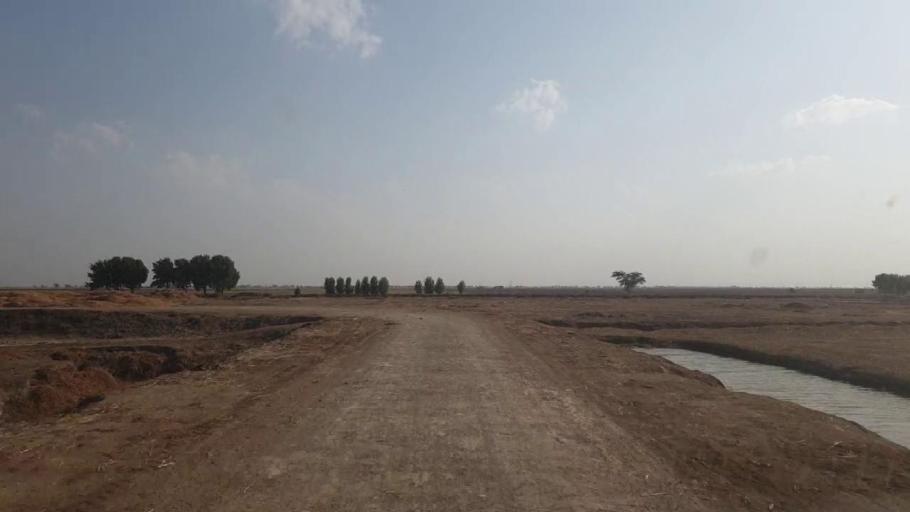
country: PK
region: Sindh
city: Kario
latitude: 24.5780
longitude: 68.5415
